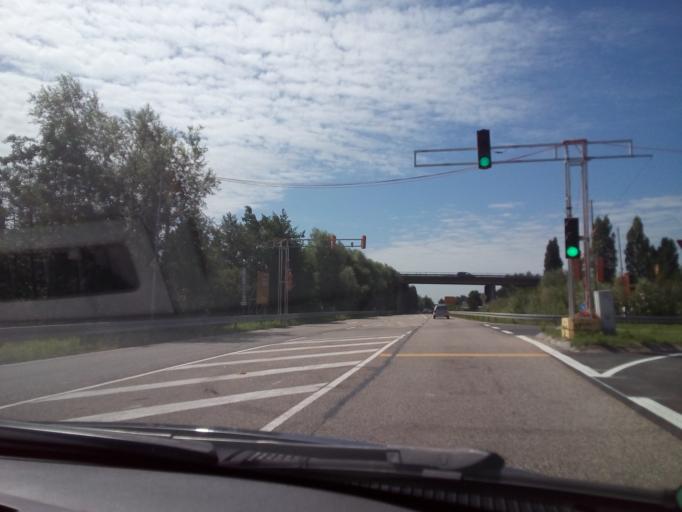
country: DE
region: Baden-Wuerttemberg
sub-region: Karlsruhe Region
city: Sinzheim
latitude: 48.7801
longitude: 8.1791
